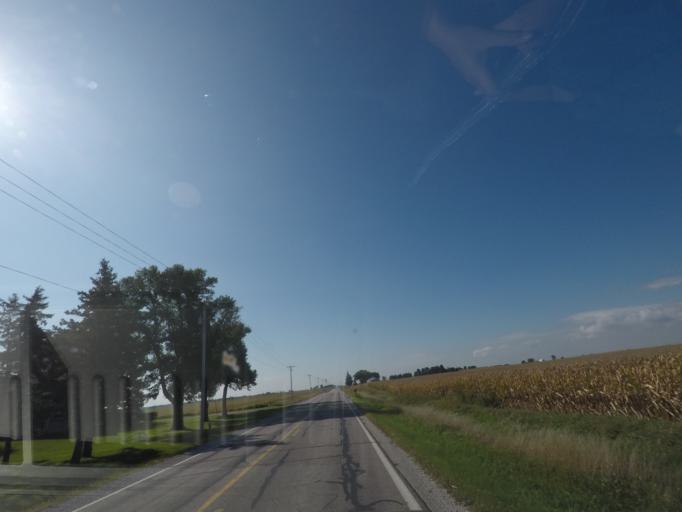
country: US
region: Iowa
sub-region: Story County
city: Nevada
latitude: 42.0444
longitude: -93.4058
